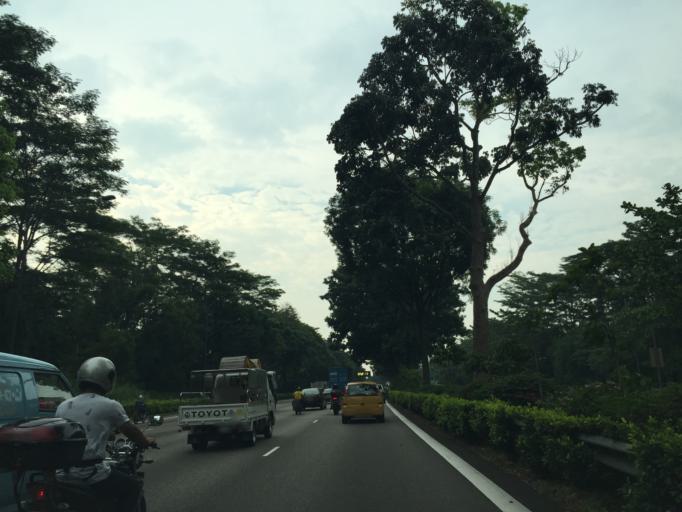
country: MY
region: Johor
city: Johor Bahru
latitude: 1.3947
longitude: 103.7739
